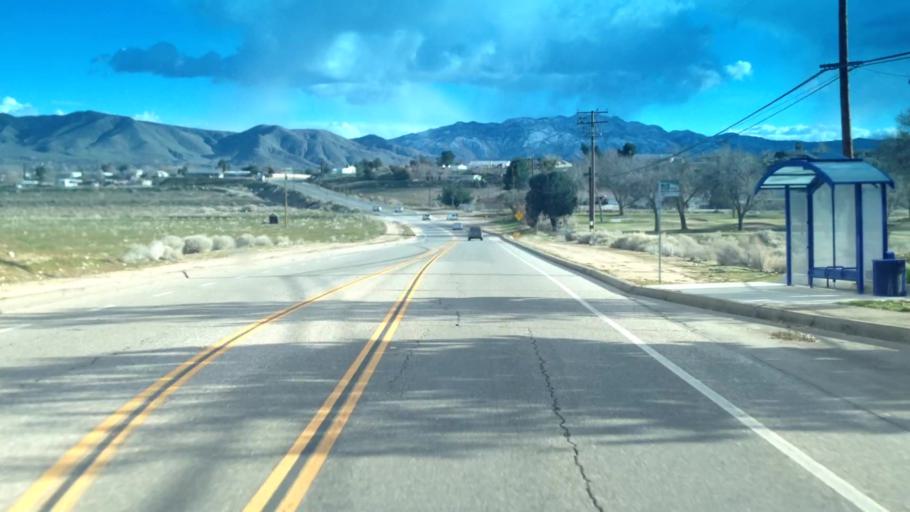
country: US
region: California
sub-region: San Bernardino County
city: Hesperia
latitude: 34.4099
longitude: -117.2532
